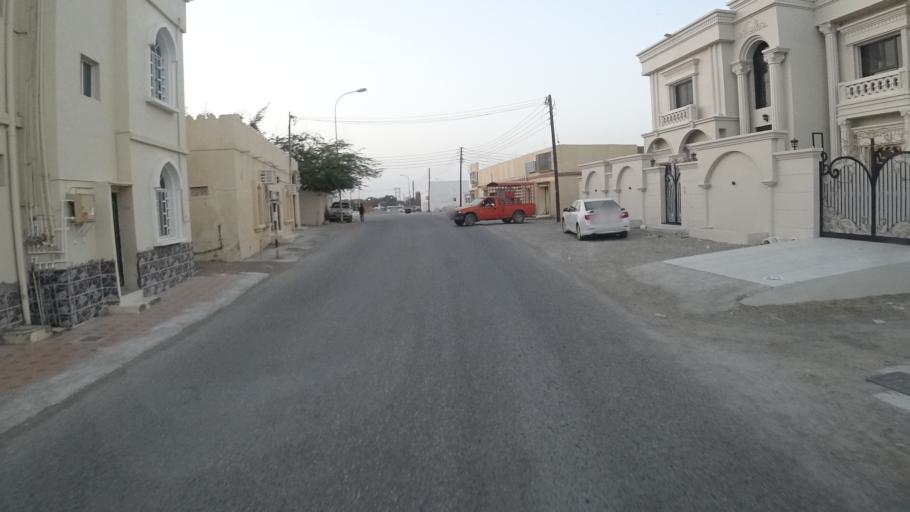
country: OM
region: Ash Sharqiyah
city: Sur
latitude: 22.5434
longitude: 59.4840
